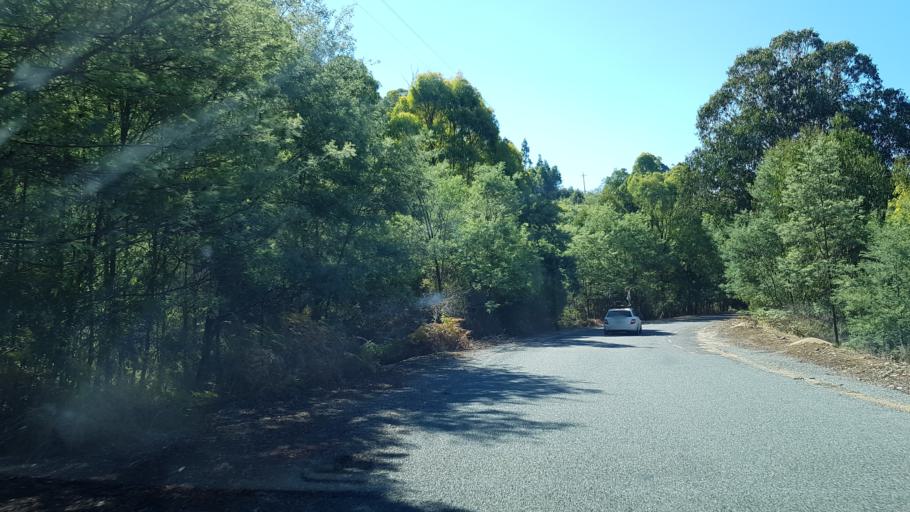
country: AU
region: Victoria
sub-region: Mansfield
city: Mansfield
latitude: -36.9091
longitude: 146.3909
